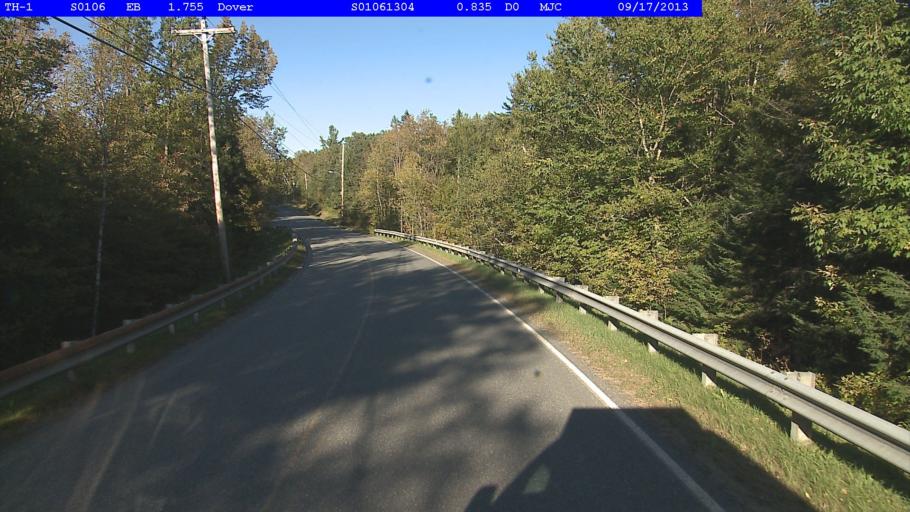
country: US
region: Vermont
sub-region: Windham County
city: Dover
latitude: 42.9288
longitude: -72.8189
